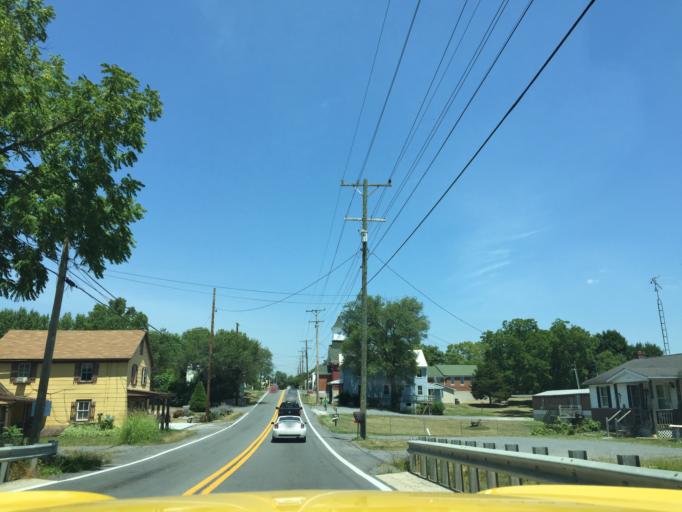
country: US
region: West Virginia
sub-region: Berkeley County
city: Inwood
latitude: 39.3713
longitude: -78.0274
